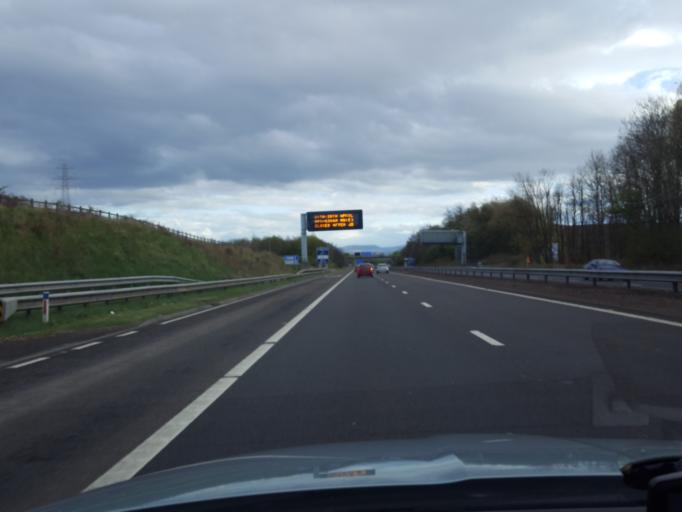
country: GB
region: Scotland
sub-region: Fife
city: Crossgates
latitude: 56.0601
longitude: -3.3872
